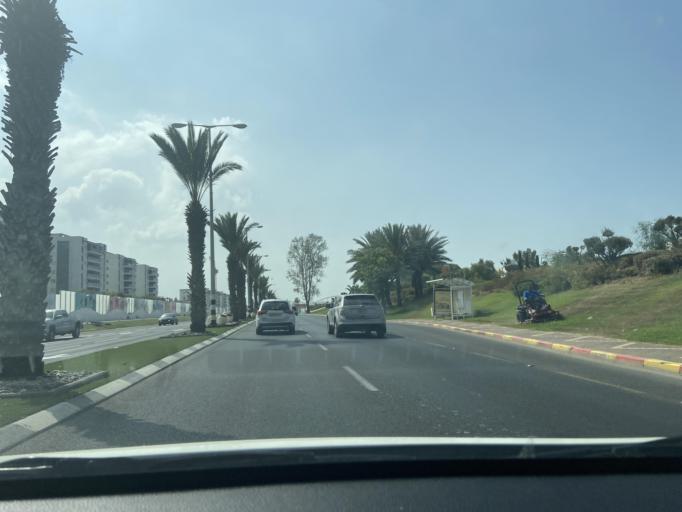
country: IL
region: Northern District
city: Nahariya
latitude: 33.0019
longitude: 35.0986
